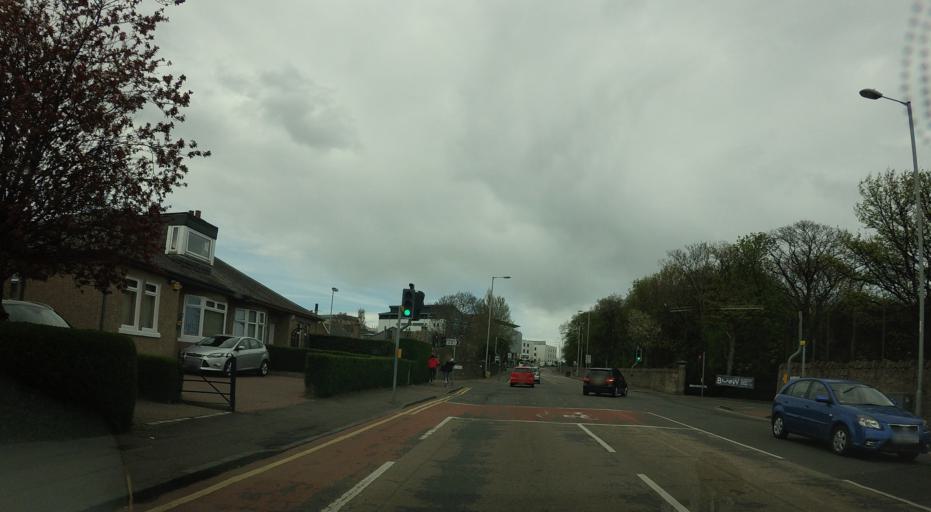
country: GB
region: Scotland
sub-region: Edinburgh
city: Edinburgh
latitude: 55.9606
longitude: -3.2292
